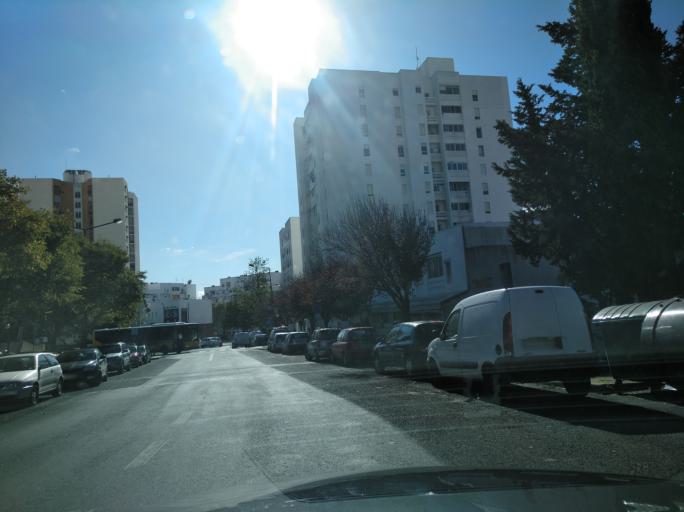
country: PT
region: Lisbon
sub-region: Lisbon
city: Lisbon
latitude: 38.7450
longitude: -9.1135
